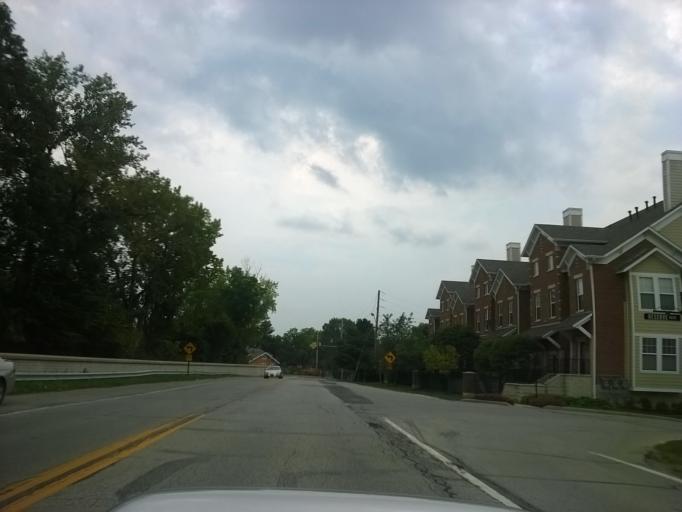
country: US
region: Indiana
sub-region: Marion County
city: Broad Ripple
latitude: 39.8757
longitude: -86.1402
